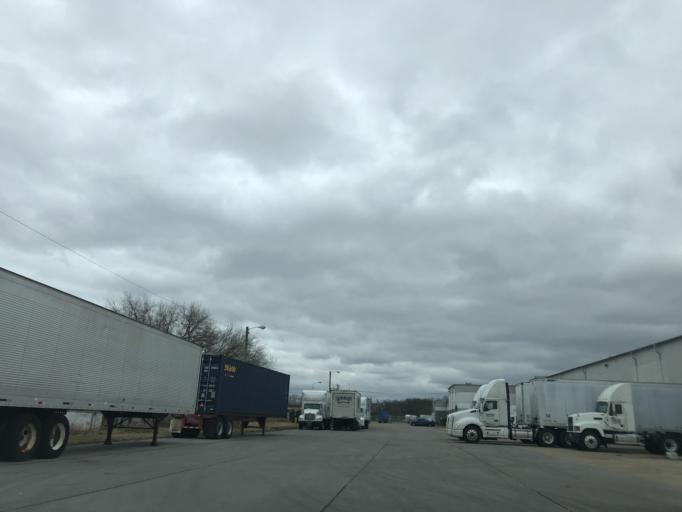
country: US
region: Tennessee
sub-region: Davidson County
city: Goodlettsville
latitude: 36.2845
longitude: -86.6971
